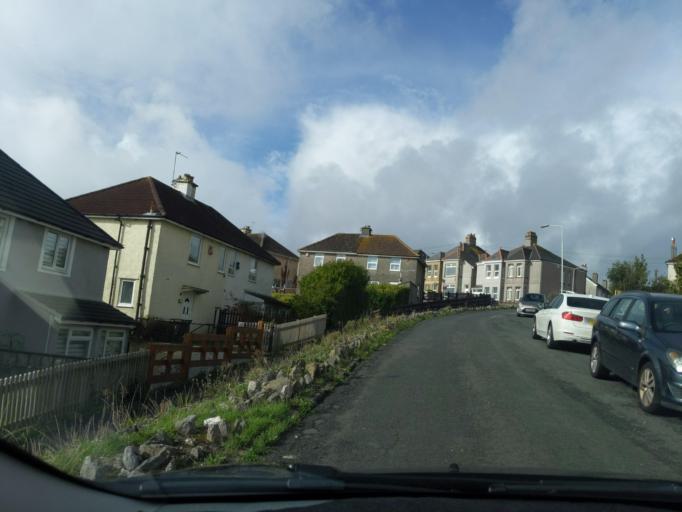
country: GB
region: England
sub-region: Cornwall
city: Torpoint
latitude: 50.4068
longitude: -4.1821
